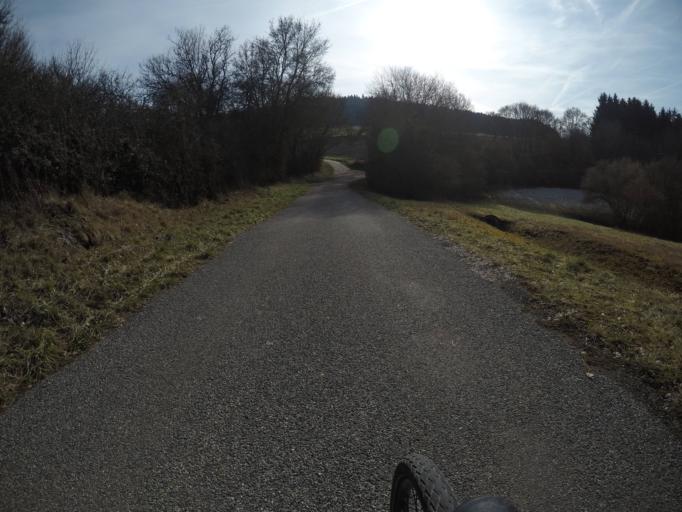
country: DE
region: Baden-Wuerttemberg
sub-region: Karlsruhe Region
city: Wildberg
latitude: 48.6412
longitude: 8.7696
